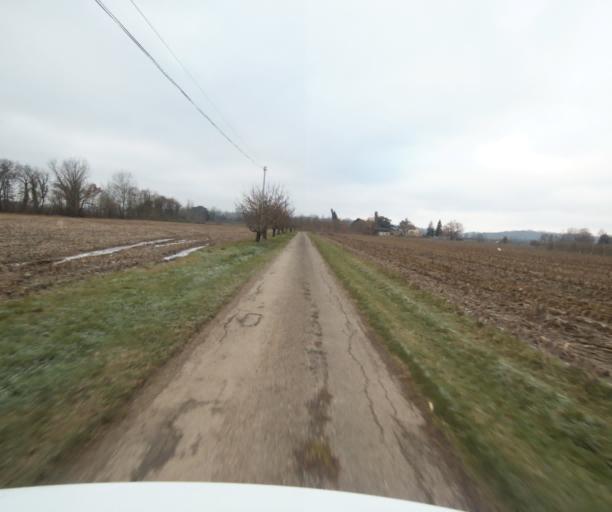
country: FR
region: Midi-Pyrenees
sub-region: Departement du Tarn-et-Garonne
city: Moissac
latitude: 44.1017
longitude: 1.1278
